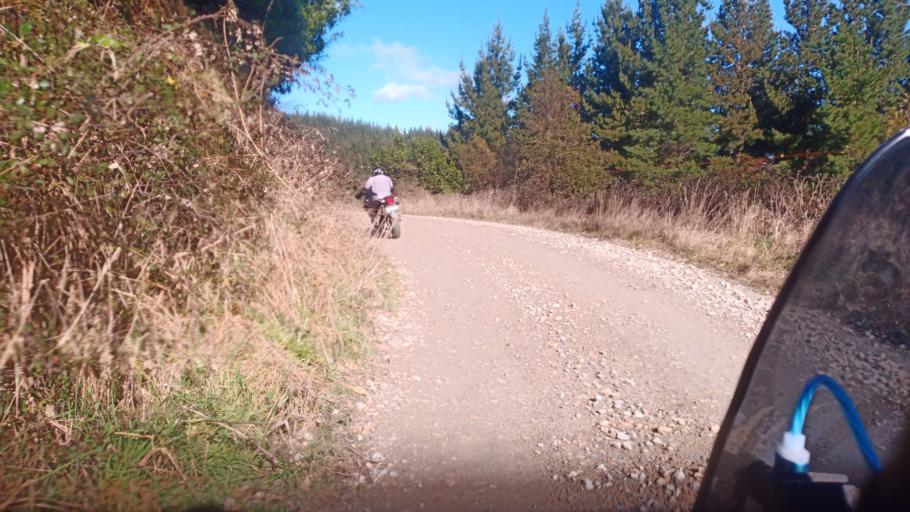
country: NZ
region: Hawke's Bay
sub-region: Wairoa District
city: Wairoa
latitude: -38.6688
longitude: 177.5442
